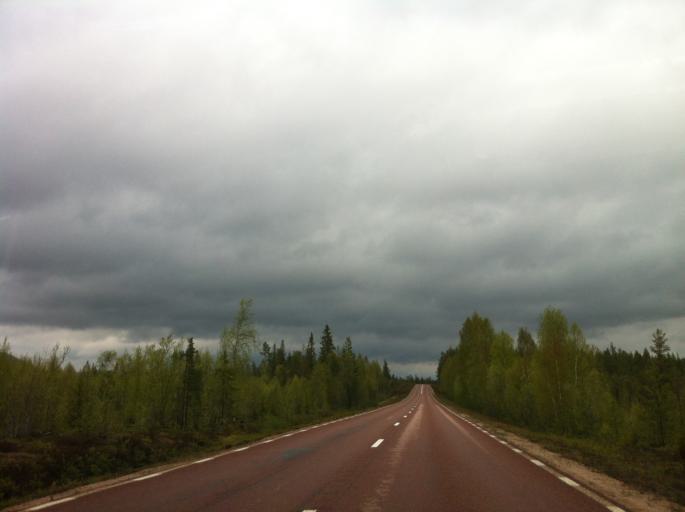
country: SE
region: Jaemtland
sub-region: Harjedalens Kommun
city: Sveg
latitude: 61.9001
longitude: 14.6226
